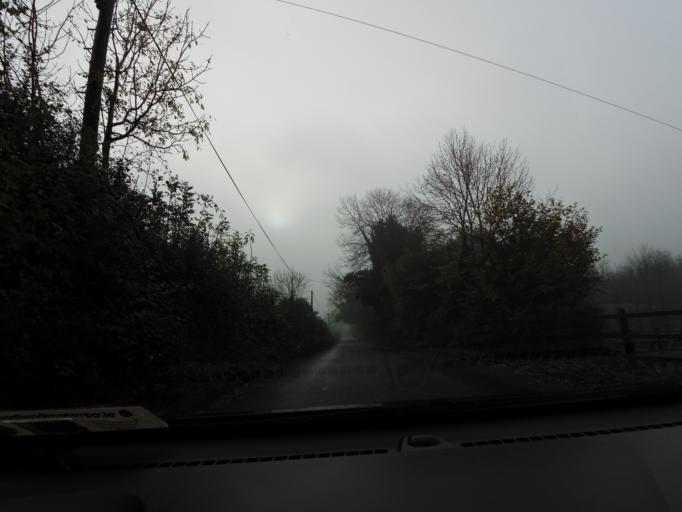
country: IE
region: Leinster
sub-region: An Iarmhi
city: Moate
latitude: 53.3885
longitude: -7.8072
